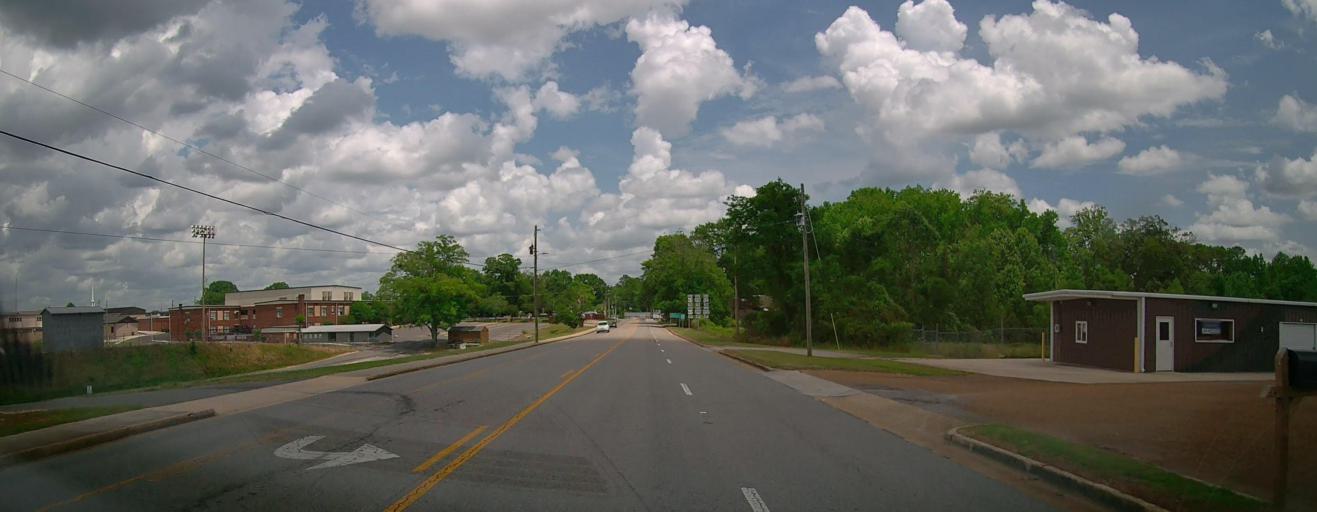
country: US
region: Alabama
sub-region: Marion County
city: Hamilton
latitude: 34.1376
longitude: -87.9936
